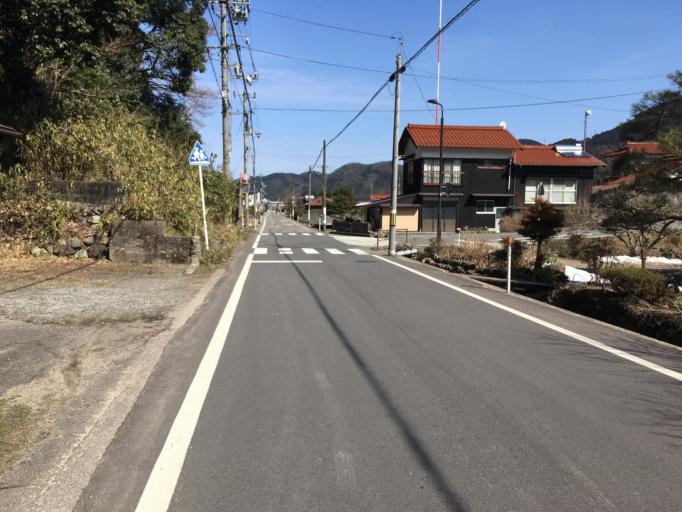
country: JP
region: Shimane
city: Masuda
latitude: 34.4552
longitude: 131.7656
